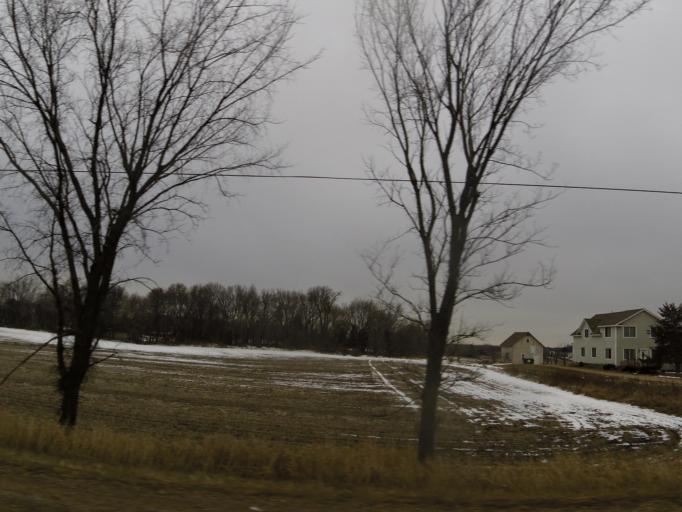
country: US
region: Minnesota
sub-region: Carver County
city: Cologne
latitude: 44.7764
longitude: -93.7042
